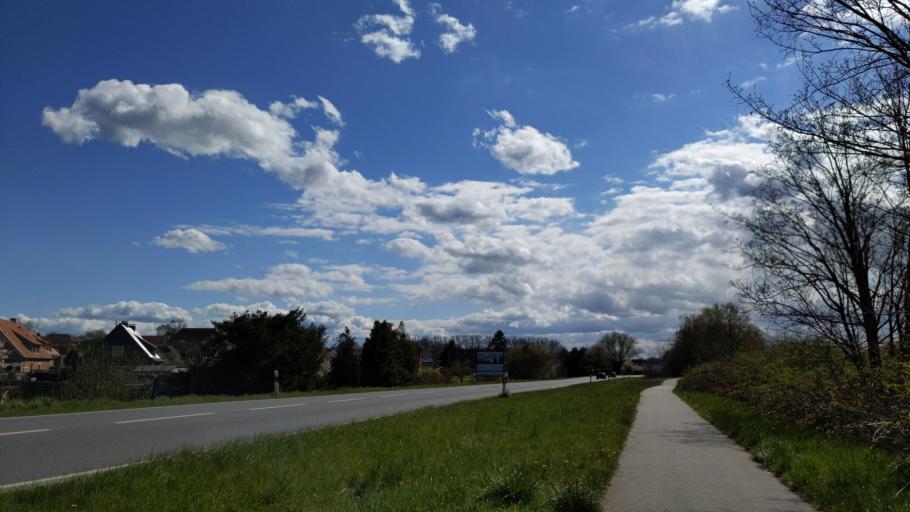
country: DE
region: Mecklenburg-Vorpommern
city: Dassow
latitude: 53.9099
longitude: 10.9707
